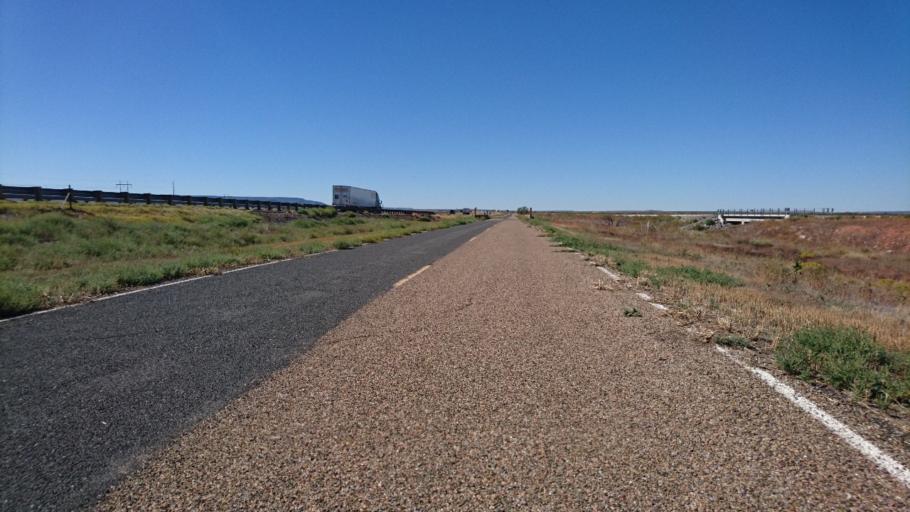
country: US
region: New Mexico
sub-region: Quay County
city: Tucumcari
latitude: 35.1036
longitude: -104.0369
